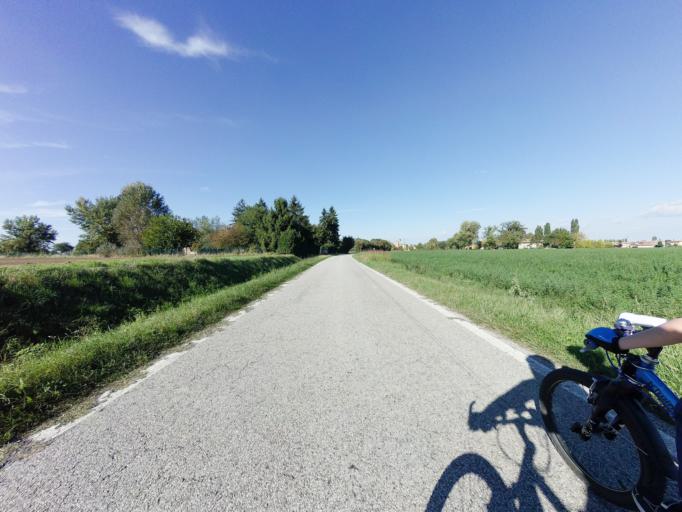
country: IT
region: Emilia-Romagna
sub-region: Provincia di Bologna
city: Bentivoglio
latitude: 44.5985
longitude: 11.4145
